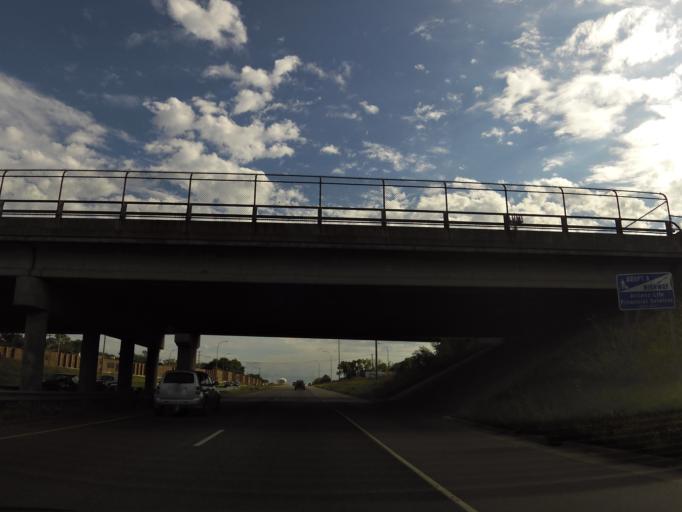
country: US
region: Minnesota
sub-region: Hennepin County
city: New Hope
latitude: 45.0224
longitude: -93.4010
